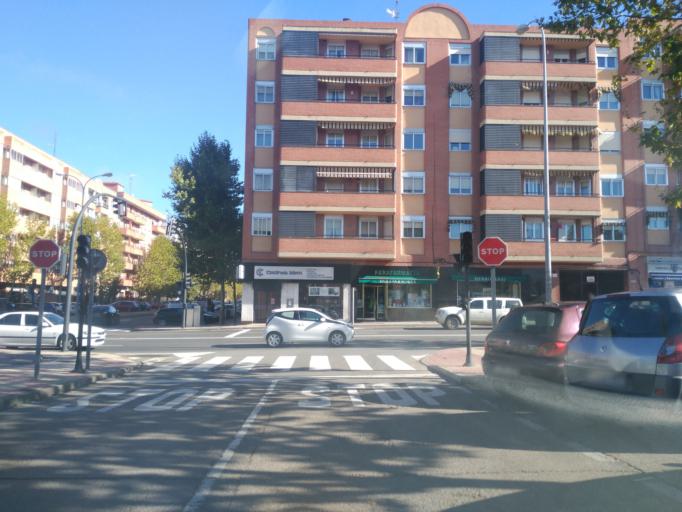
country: ES
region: Castille and Leon
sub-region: Provincia de Salamanca
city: Salamanca
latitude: 40.9707
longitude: -5.6442
